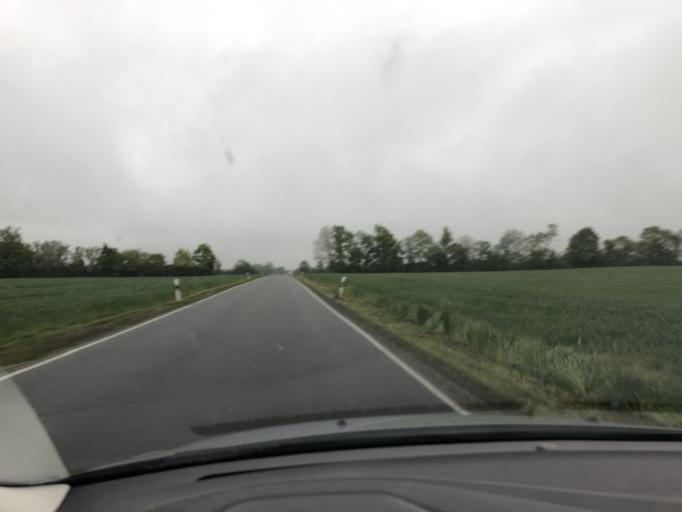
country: DE
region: Saxony
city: Jesewitz
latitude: 51.4347
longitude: 12.5309
